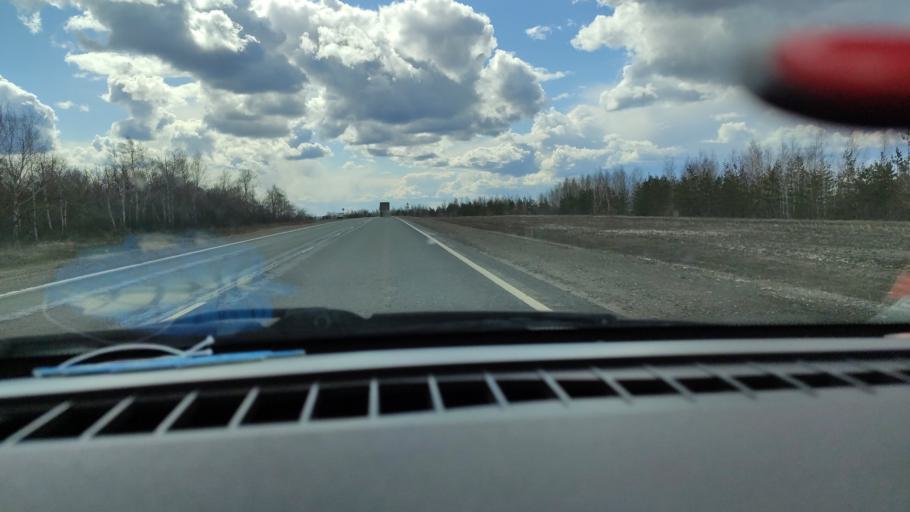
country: RU
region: Samara
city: Syzran'
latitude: 52.8631
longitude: 48.2675
